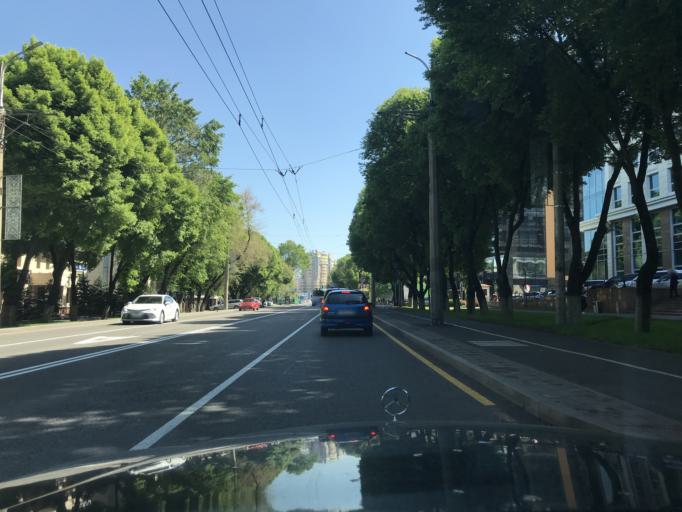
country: KZ
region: Almaty Qalasy
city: Almaty
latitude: 43.2297
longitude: 76.9323
